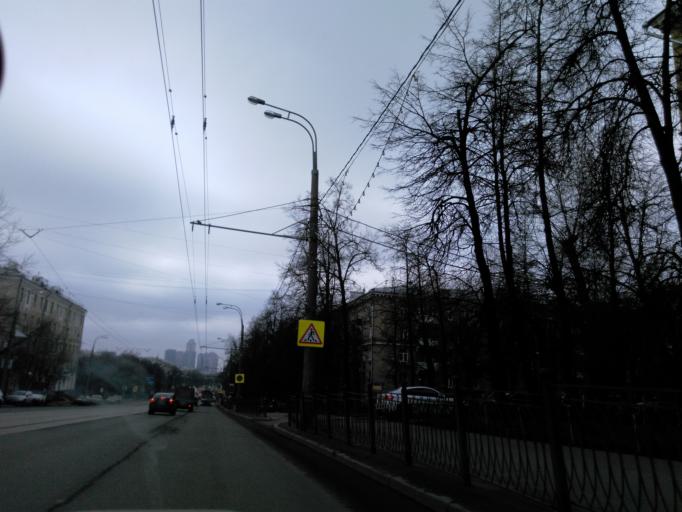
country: RU
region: Moscow
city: Pokrovskoye-Streshnevo
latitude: 55.8317
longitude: 37.4532
